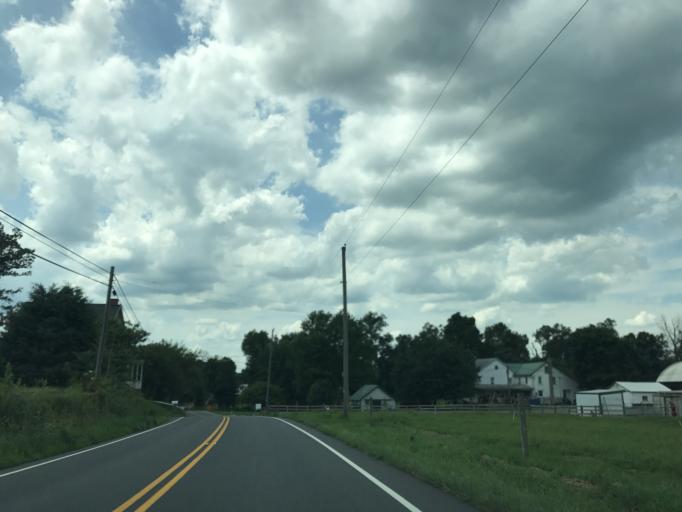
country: US
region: Pennsylvania
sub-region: Lancaster County
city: Mount Joy
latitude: 40.1856
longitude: -76.5128
